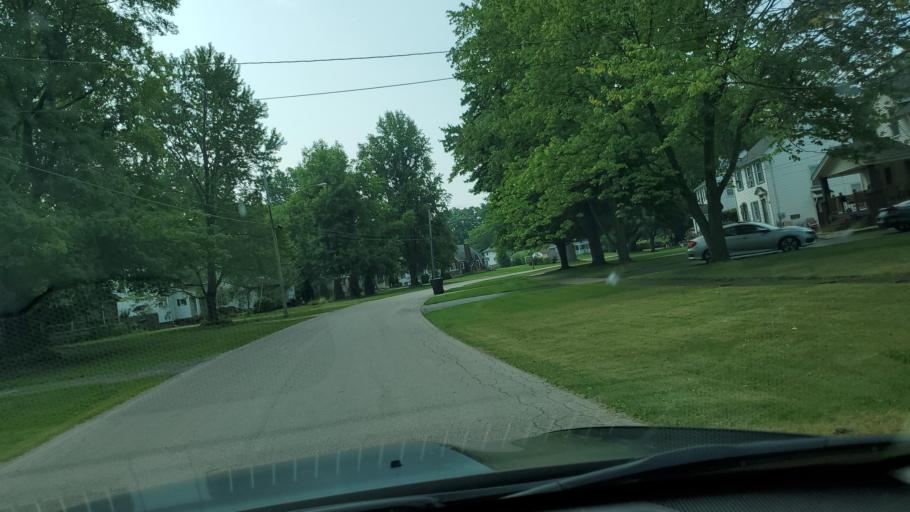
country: US
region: Ohio
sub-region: Trumbull County
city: Bolindale
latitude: 41.2265
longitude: -80.7812
